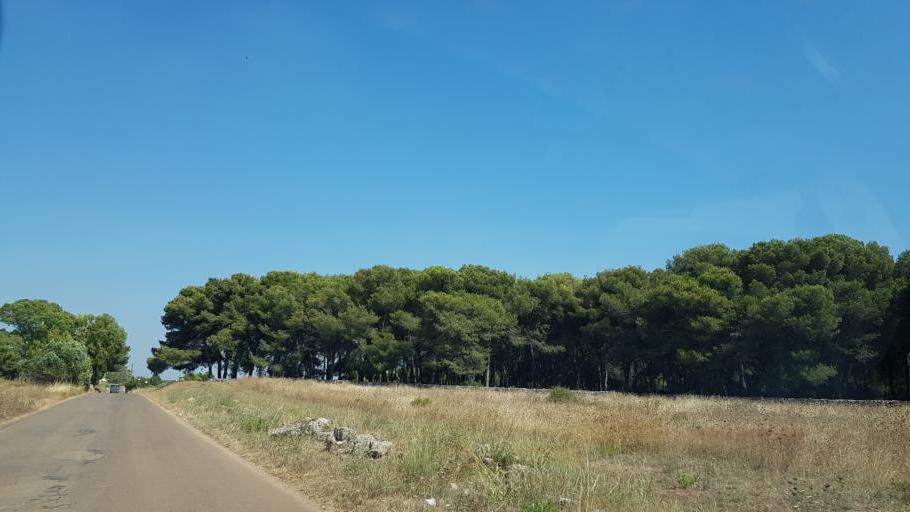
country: IT
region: Apulia
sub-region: Provincia di Lecce
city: Nardo
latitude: 40.1734
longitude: 17.9554
